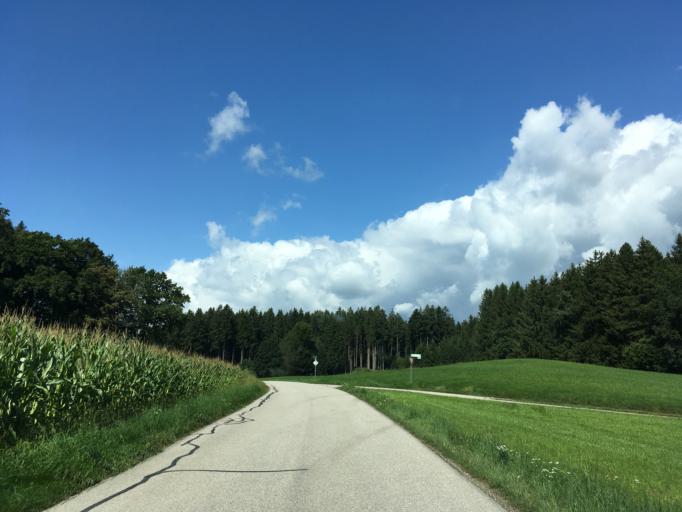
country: DE
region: Bavaria
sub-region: Upper Bavaria
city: Pittenhart
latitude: 47.9728
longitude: 12.3693
